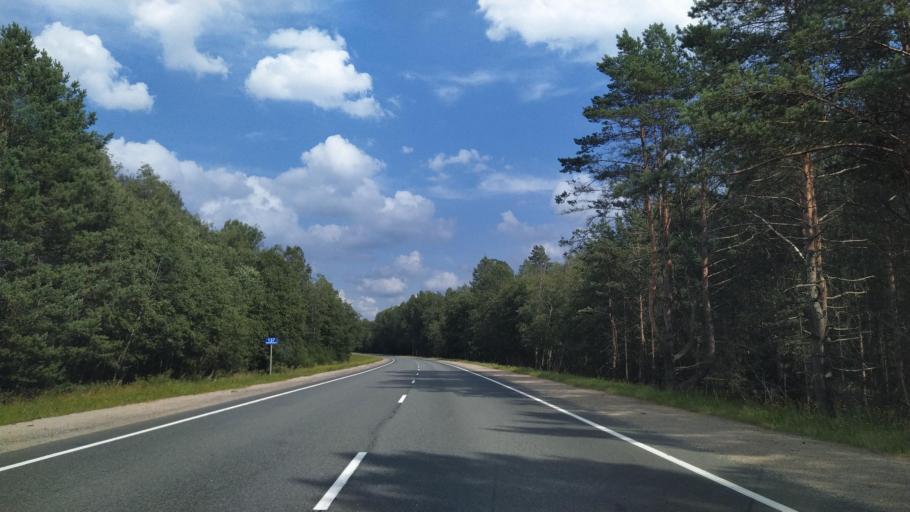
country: RU
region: Pskov
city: Porkhov
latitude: 57.8639
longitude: 29.5903
